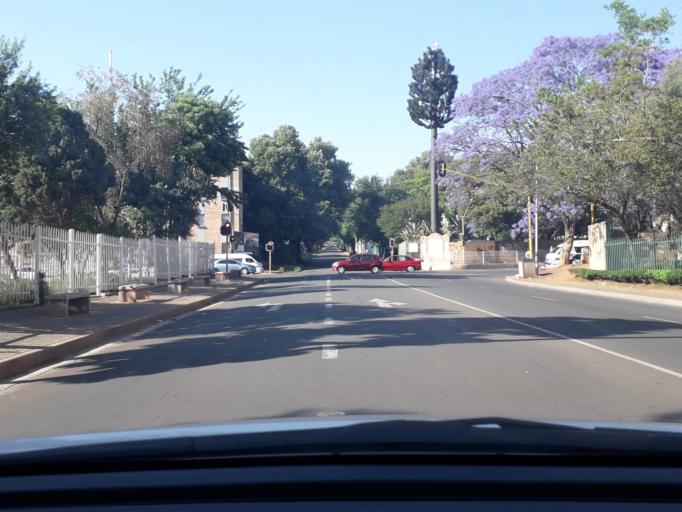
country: ZA
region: Gauteng
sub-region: City of Johannesburg Metropolitan Municipality
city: Johannesburg
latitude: -26.1830
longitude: 28.0064
